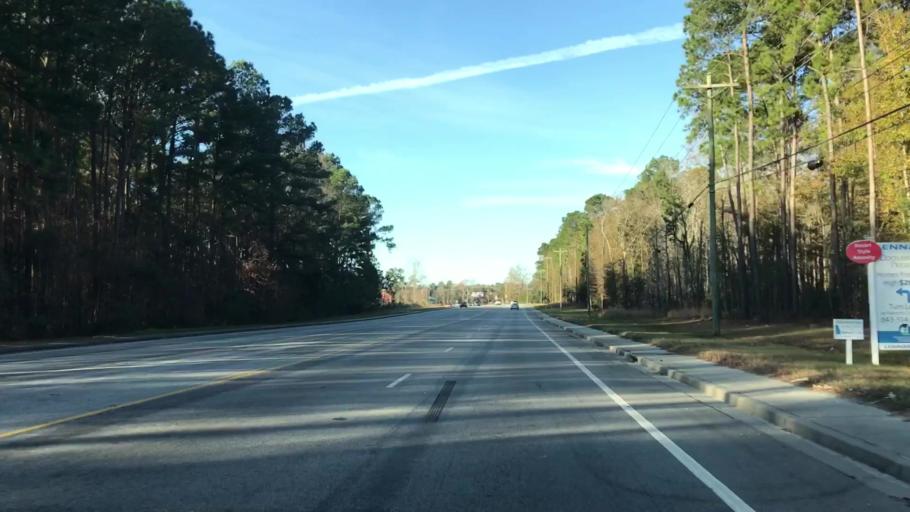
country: US
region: South Carolina
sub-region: Berkeley County
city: Ladson
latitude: 32.9833
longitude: -80.1216
